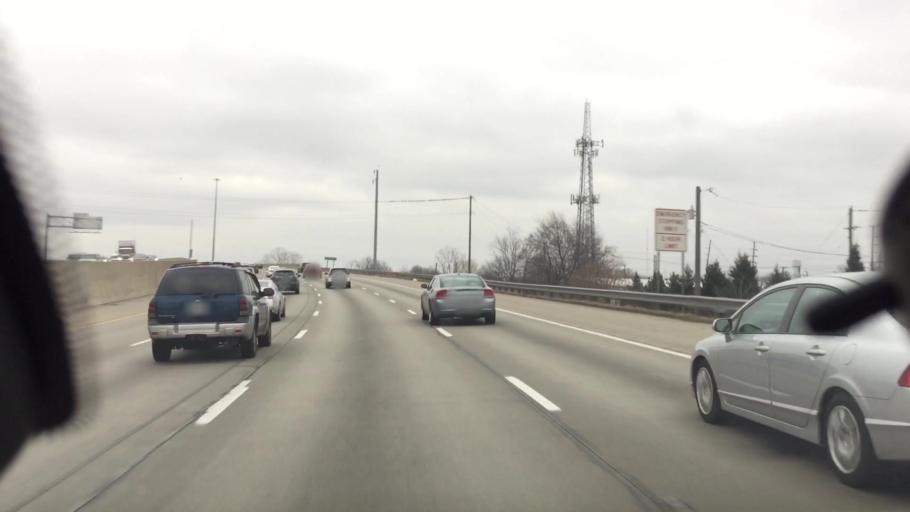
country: US
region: Indiana
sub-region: Marion County
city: Warren Park
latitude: 39.7970
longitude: -86.1046
